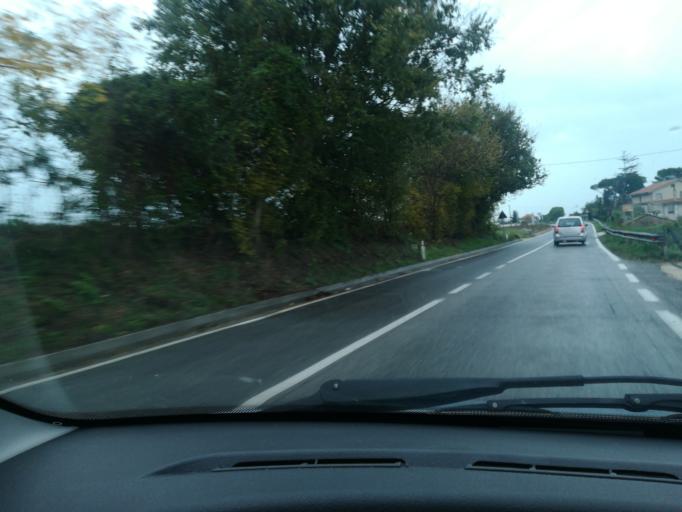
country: IT
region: The Marches
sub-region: Provincia di Macerata
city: Santa Maria Apparente
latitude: 43.2946
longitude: 13.6716
